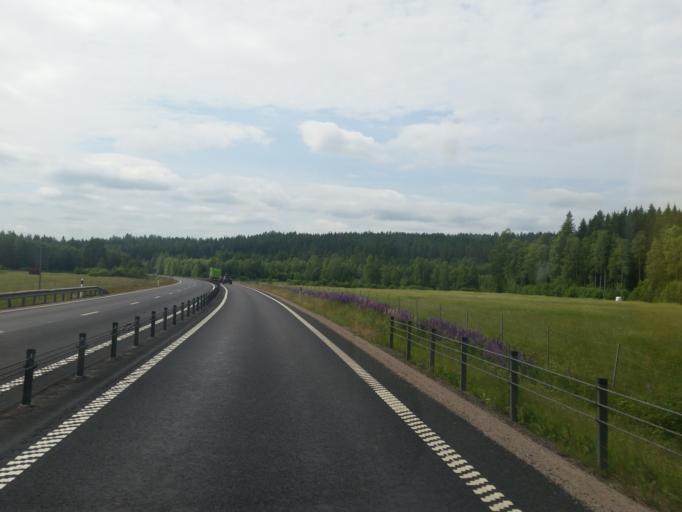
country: SE
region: Dalarna
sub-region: Borlange Kommun
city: Borlaenge
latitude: 60.4585
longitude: 15.3757
